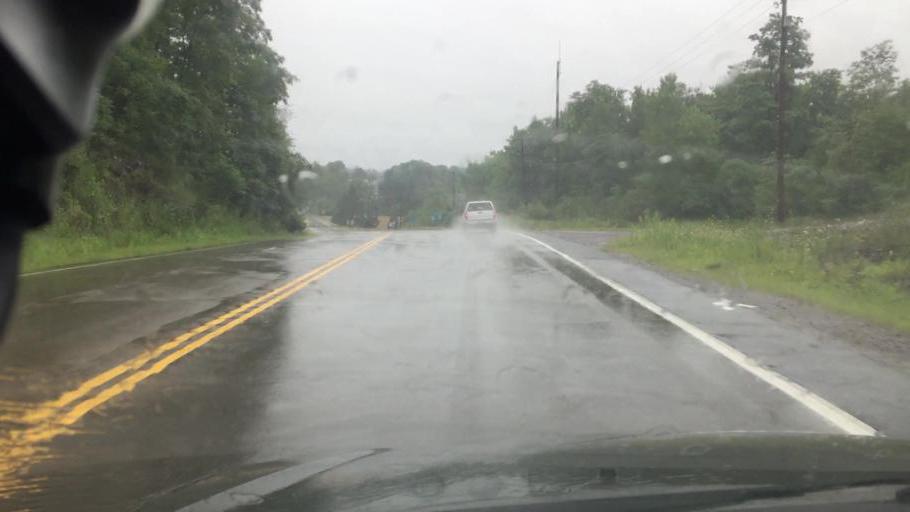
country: US
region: Pennsylvania
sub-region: Luzerne County
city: White Haven
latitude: 41.0518
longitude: -75.7759
